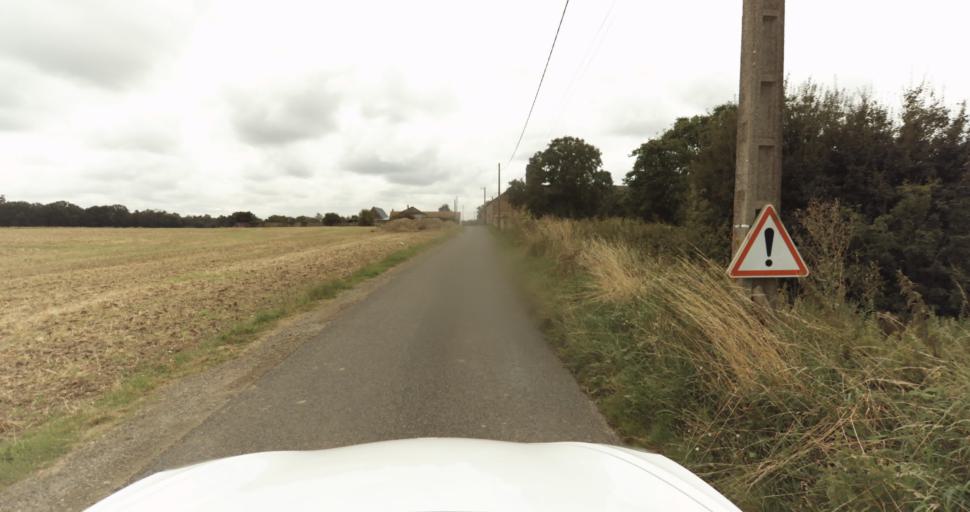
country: FR
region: Haute-Normandie
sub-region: Departement de l'Eure
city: Saint-Sebastien-de-Morsent
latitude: 49.0195
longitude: 1.0607
